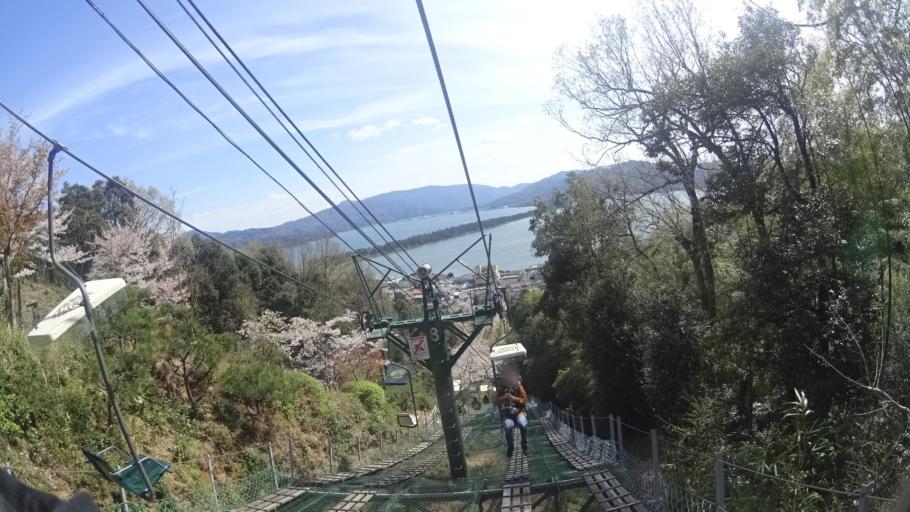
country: JP
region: Kyoto
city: Miyazu
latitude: 35.5855
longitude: 135.1955
